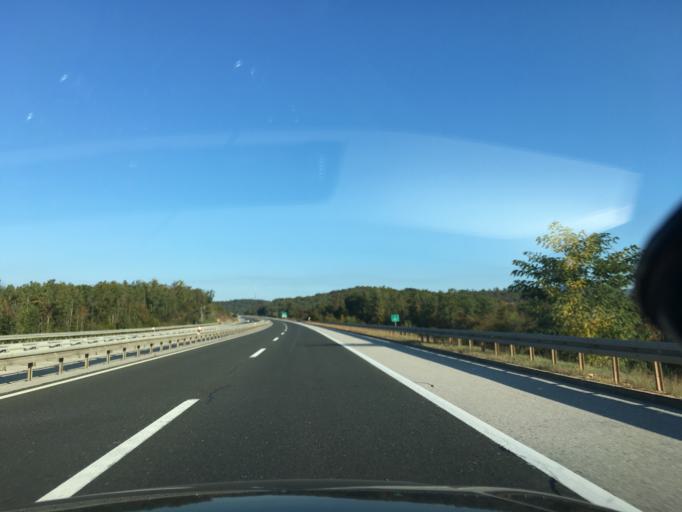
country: HR
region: Licko-Senjska
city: Gospic
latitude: 44.7275
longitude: 15.3849
